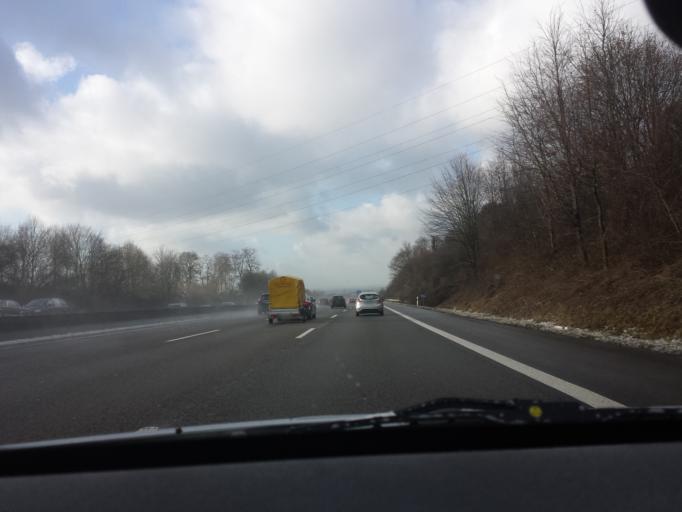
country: DE
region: North Rhine-Westphalia
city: Haan
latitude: 51.2014
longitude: 6.9966
